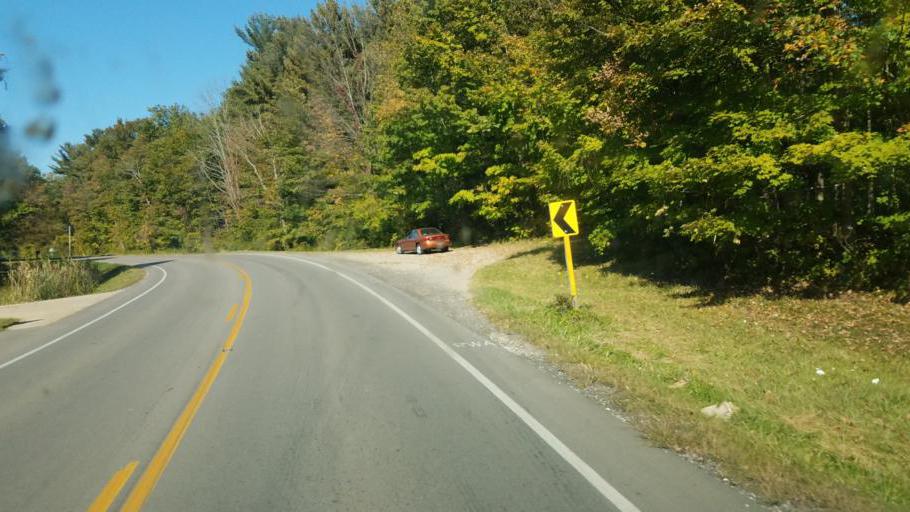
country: US
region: Ohio
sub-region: Richland County
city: Lexington
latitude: 40.7068
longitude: -82.6447
